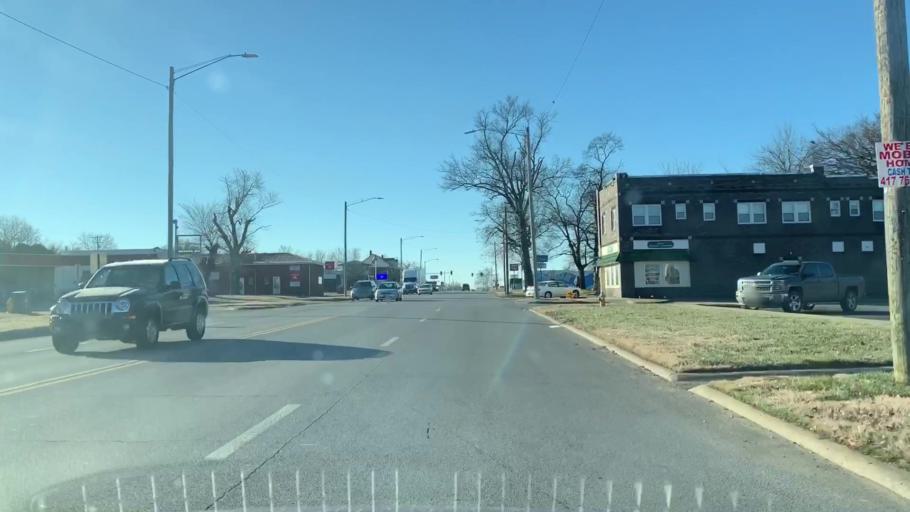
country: US
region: Kansas
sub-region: Crawford County
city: Pittsburg
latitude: 37.4027
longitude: -94.7050
